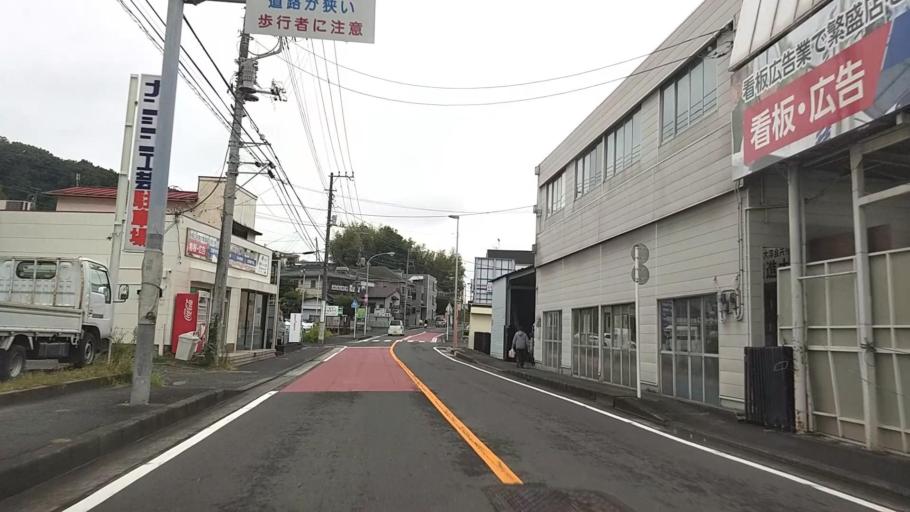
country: JP
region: Kanagawa
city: Fujisawa
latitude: 35.3947
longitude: 139.5362
